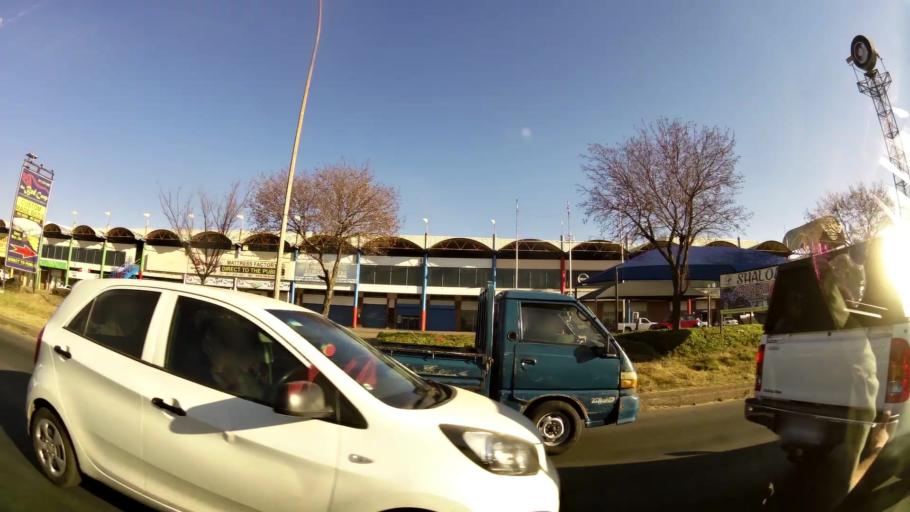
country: ZA
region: Gauteng
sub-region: City of Johannesburg Metropolitan Municipality
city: Johannesburg
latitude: -26.2027
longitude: 27.9710
